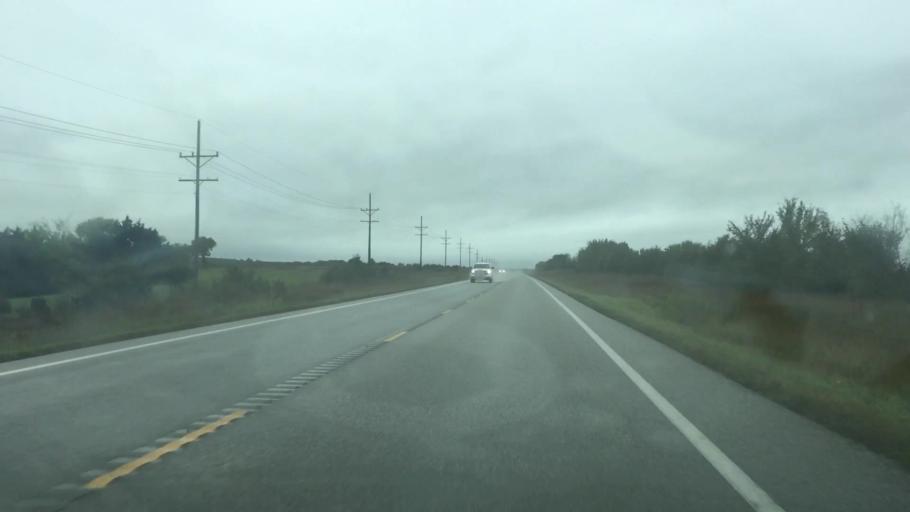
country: US
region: Kansas
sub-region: Anderson County
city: Garnett
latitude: 38.3483
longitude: -95.1598
